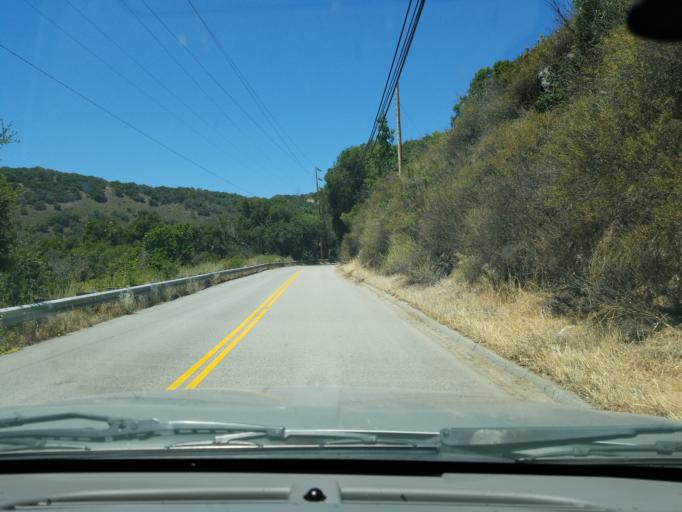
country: US
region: California
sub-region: Monterey County
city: Carmel Valley Village
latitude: 36.4634
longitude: -121.7120
